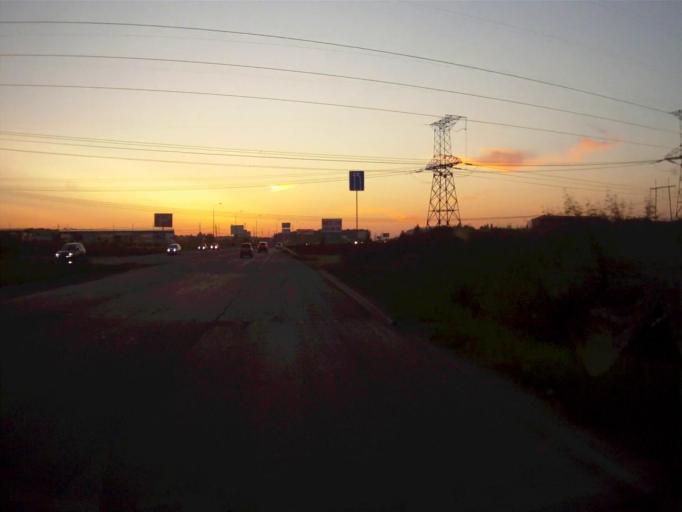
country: RU
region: Chelyabinsk
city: Roshchino
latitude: 55.1793
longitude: 61.2563
